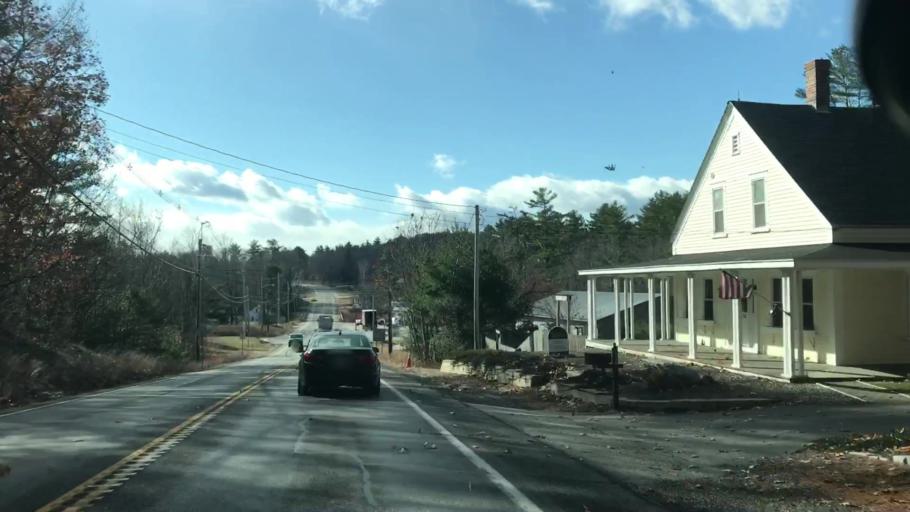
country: US
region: New Hampshire
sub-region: Carroll County
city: Wolfeboro
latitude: 43.6203
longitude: -71.1706
